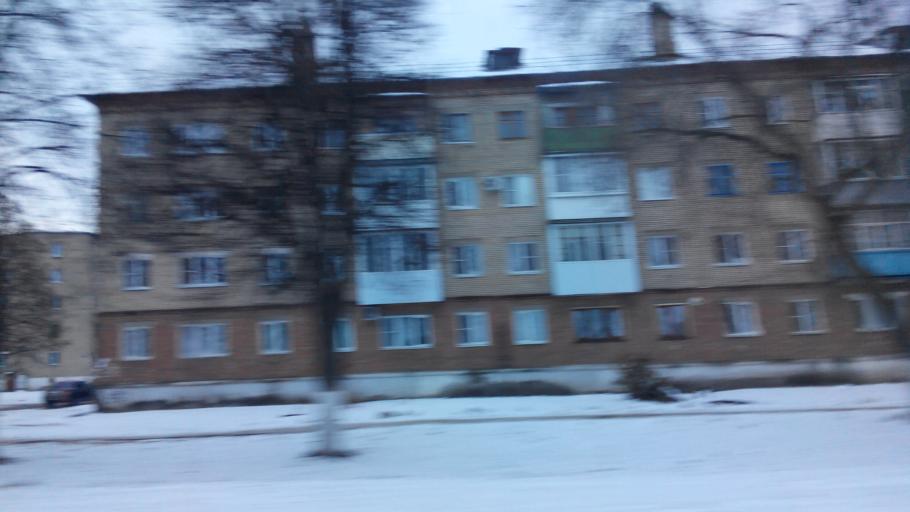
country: RU
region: Tula
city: Uzlovaya
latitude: 53.9789
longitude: 38.1905
